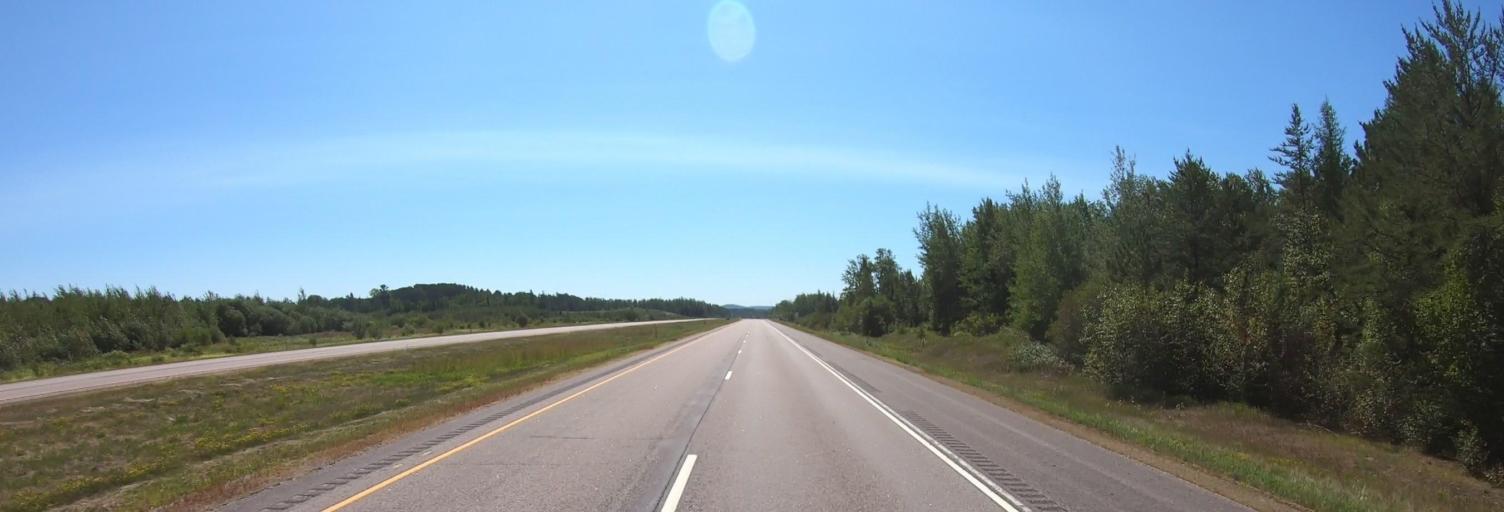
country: US
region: Minnesota
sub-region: Saint Louis County
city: Parkville
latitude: 47.6458
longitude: -92.5666
